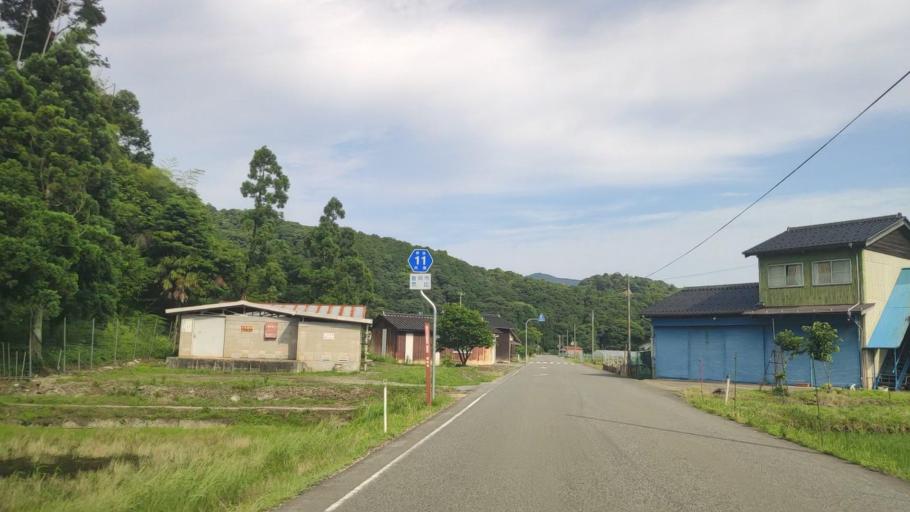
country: JP
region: Hyogo
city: Toyooka
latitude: 35.6329
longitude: 134.8399
